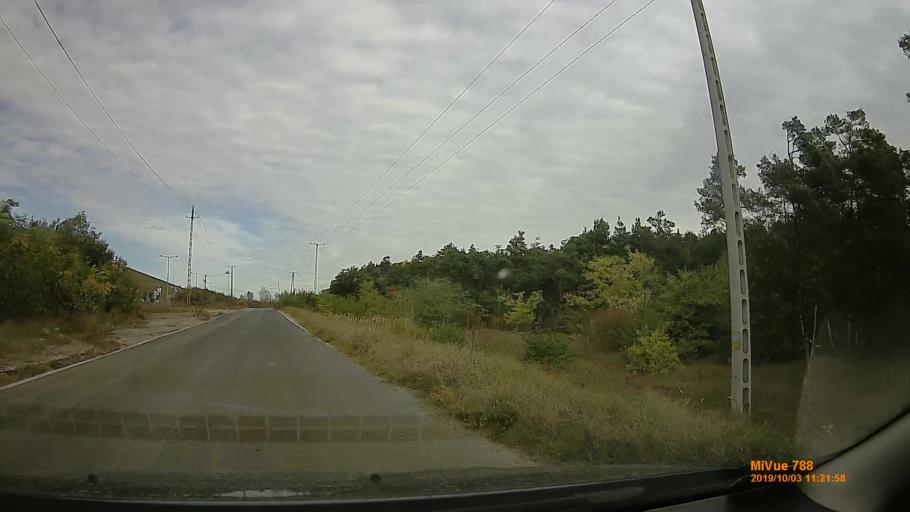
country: HU
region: Pest
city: Fot
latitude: 47.6427
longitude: 19.1742
